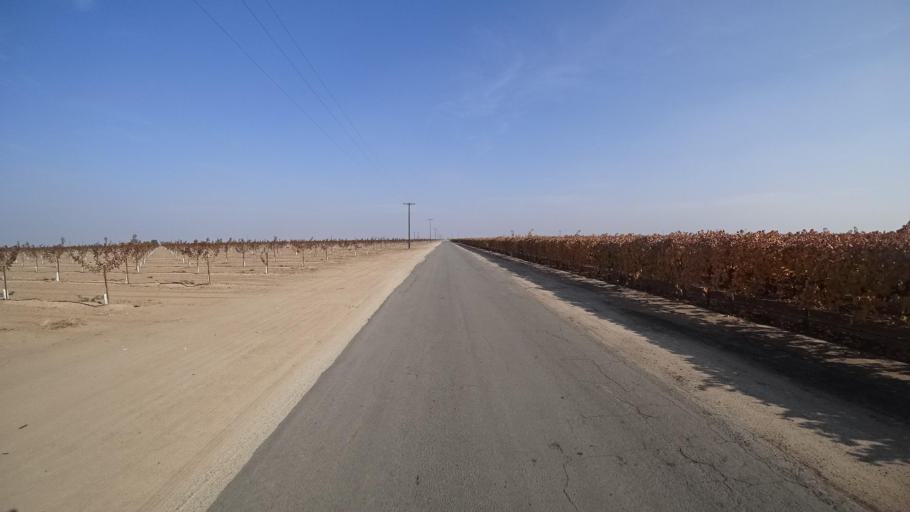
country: US
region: California
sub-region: Tulare County
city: Richgrove
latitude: 35.7762
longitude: -119.1203
